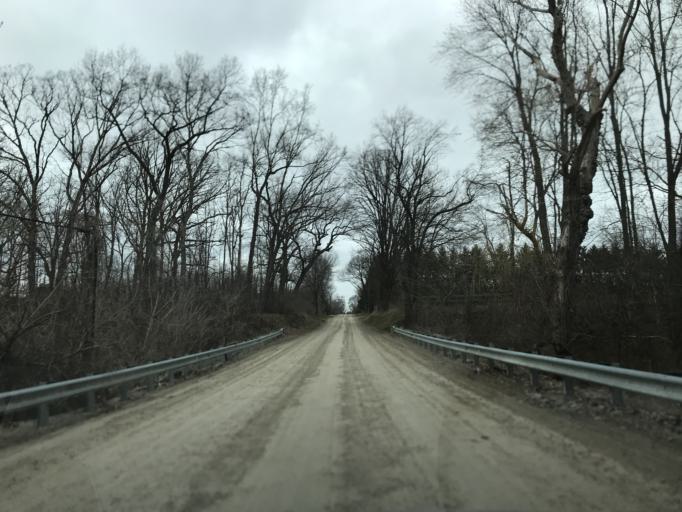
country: US
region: Michigan
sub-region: Oakland County
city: South Lyon
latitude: 42.4884
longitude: -83.6686
